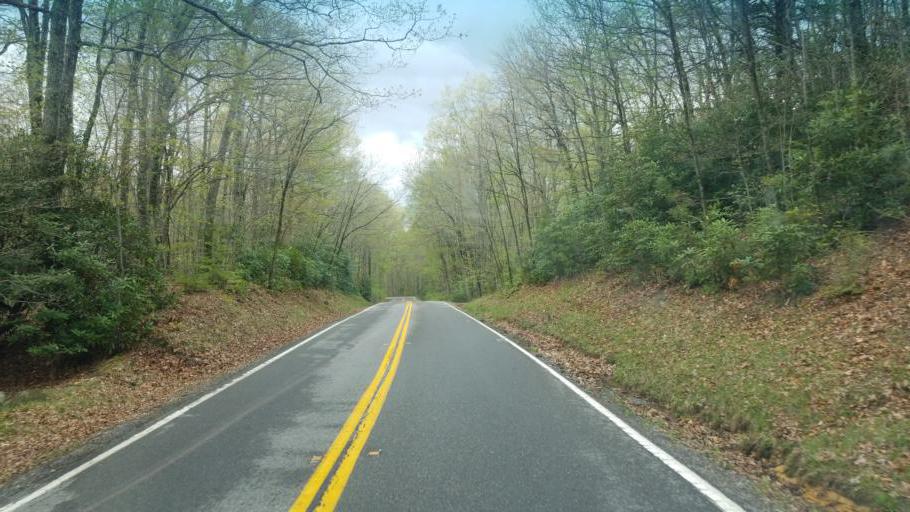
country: US
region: Virginia
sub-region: Tazewell County
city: Tazewell
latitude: 36.9929
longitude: -81.5321
